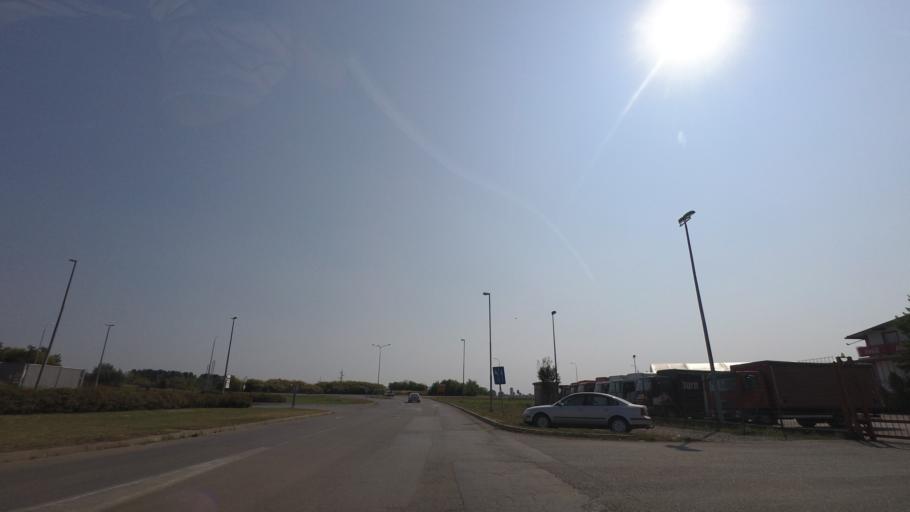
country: HR
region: Pozesko-Slavonska
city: Vidovci
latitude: 45.3380
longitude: 17.7069
